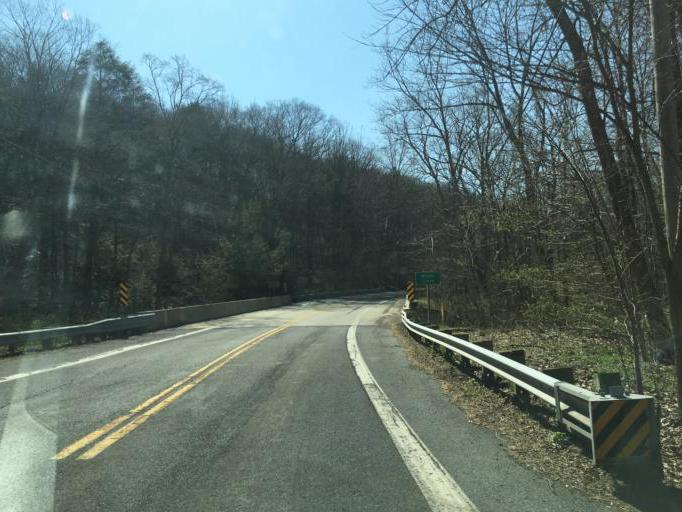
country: US
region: Maryland
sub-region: Frederick County
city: Myersville
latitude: 39.5695
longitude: -77.5325
